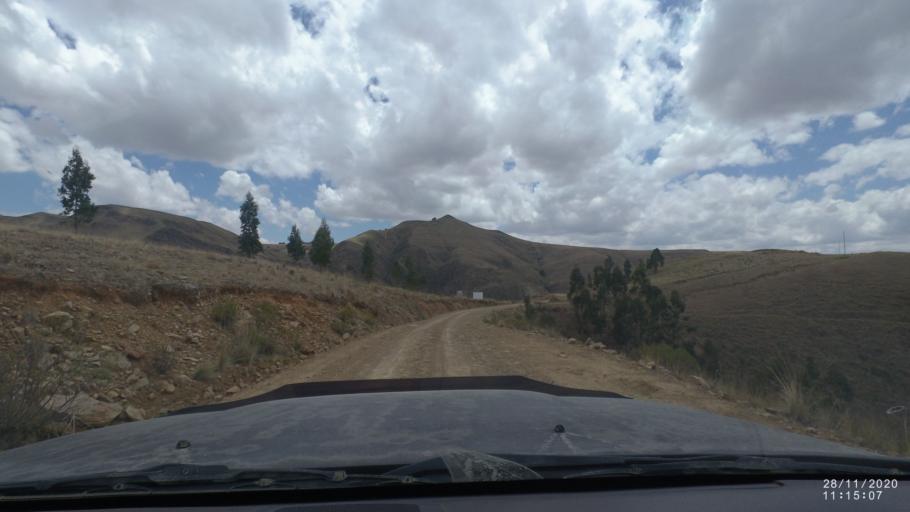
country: BO
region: Cochabamba
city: Tarata
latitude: -17.7451
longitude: -66.0919
